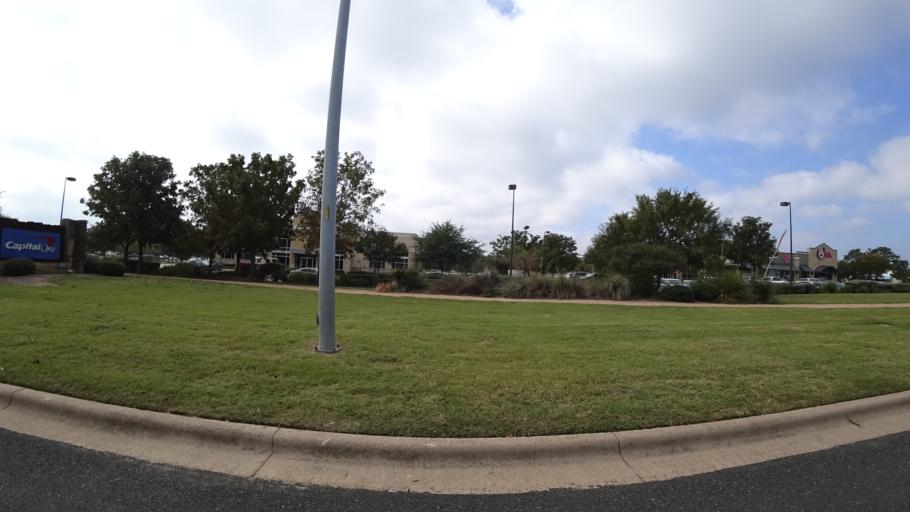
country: US
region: Texas
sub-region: Travis County
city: Shady Hollow
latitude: 30.2226
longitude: -97.8397
